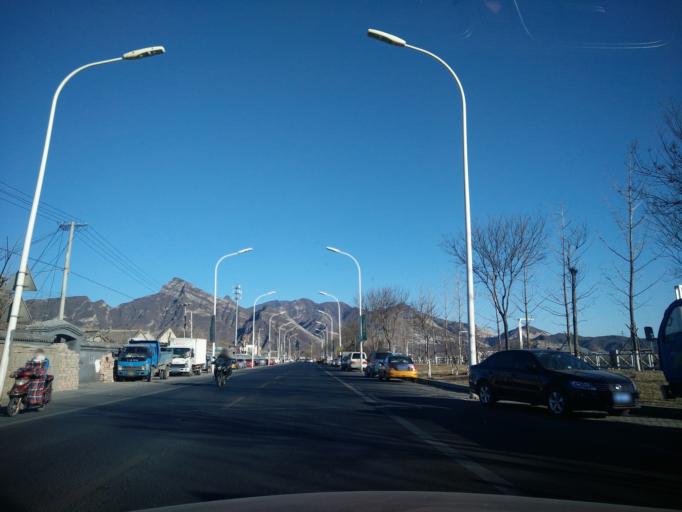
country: CN
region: Beijing
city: Junzhuang
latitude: 39.9828
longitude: 116.0817
